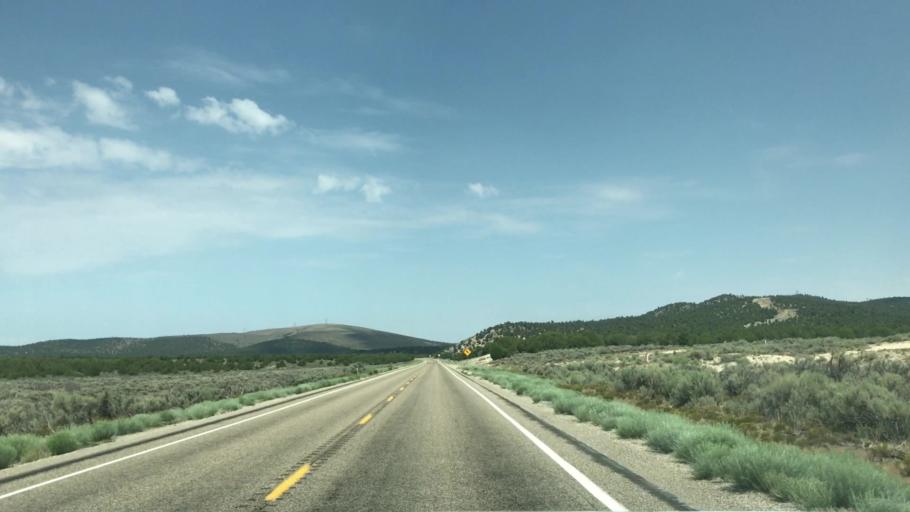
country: US
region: Nevada
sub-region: White Pine County
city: Ely
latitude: 39.3755
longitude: -115.0615
